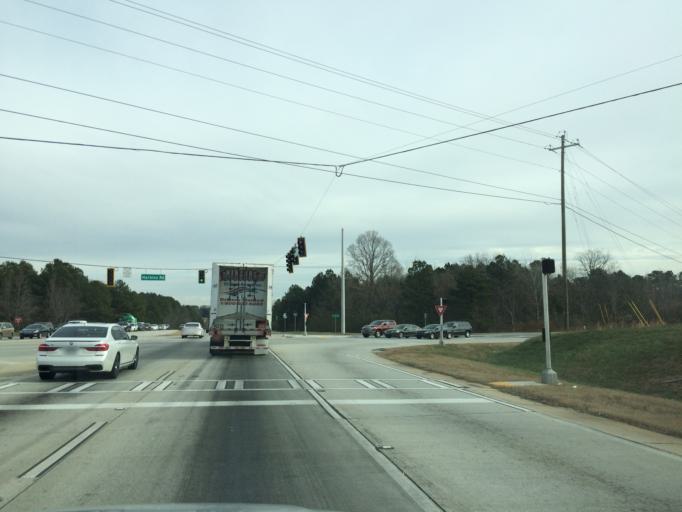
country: US
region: Georgia
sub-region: Gwinnett County
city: Dacula
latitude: 33.9735
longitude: -83.8918
